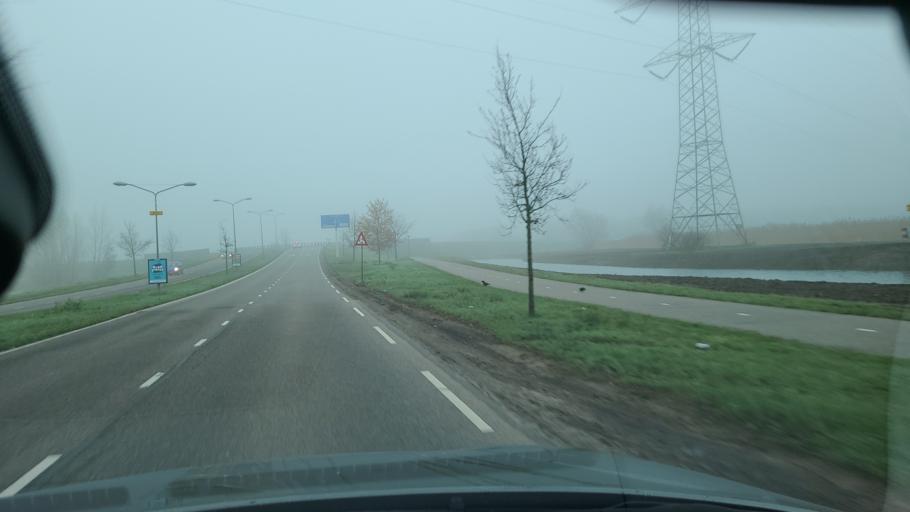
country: NL
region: North Brabant
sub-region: Gemeente 's-Hertogenbosch
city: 's-Hertogenbosch
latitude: 51.7253
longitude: 5.3460
